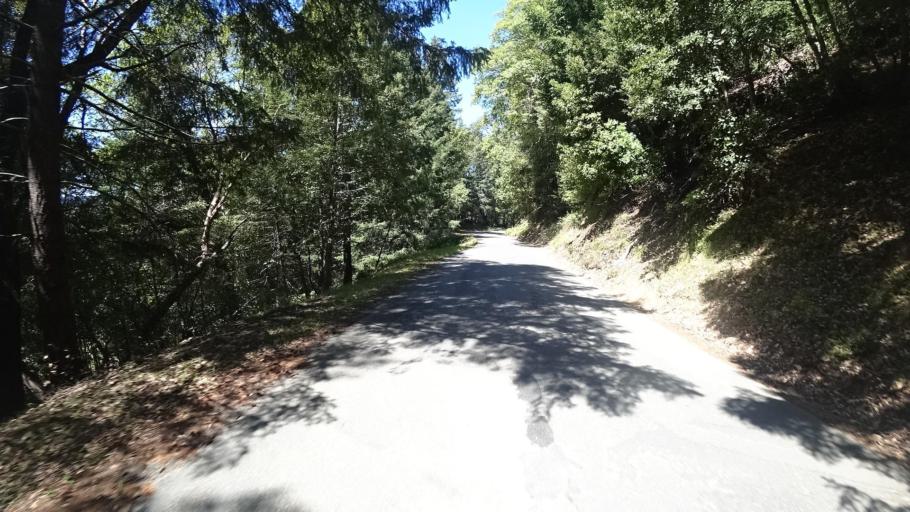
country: US
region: California
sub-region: Humboldt County
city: Redway
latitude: 40.1075
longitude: -123.9552
